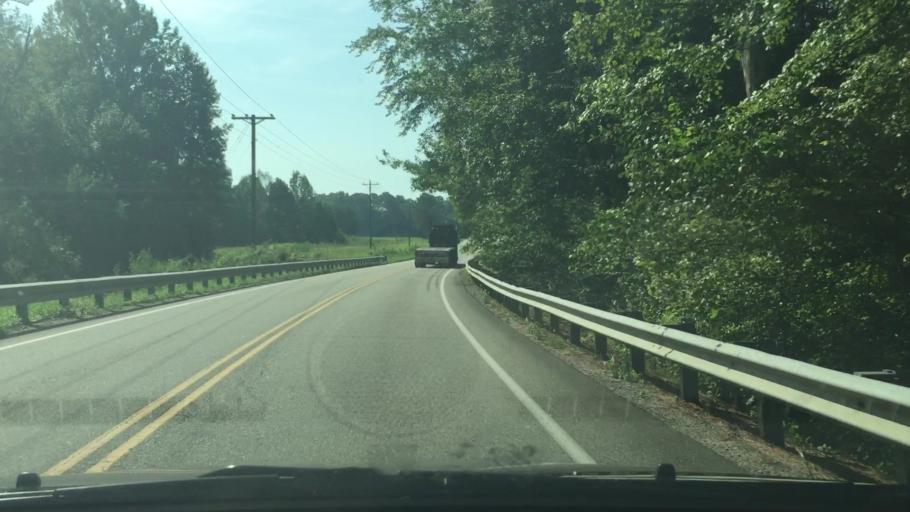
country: US
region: Virginia
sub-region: Sussex County
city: Sussex
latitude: 37.0477
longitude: -77.3146
